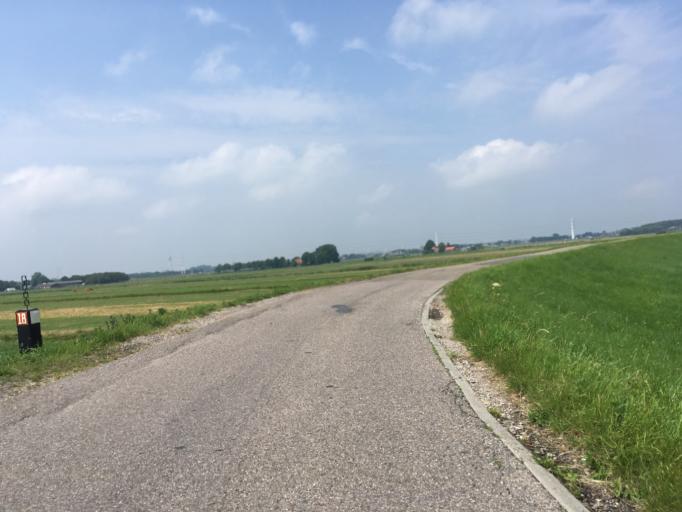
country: NL
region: North Holland
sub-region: Gemeente Haarlem
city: Haarlem
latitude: 52.3958
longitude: 4.7232
